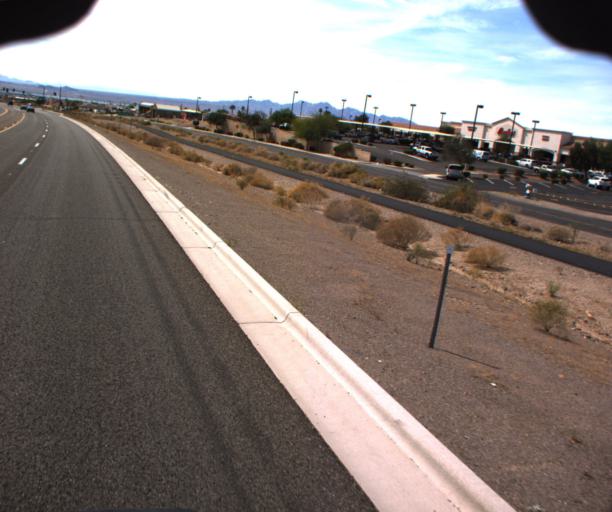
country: US
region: Arizona
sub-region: Mohave County
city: Lake Havasu City
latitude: 34.4577
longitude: -114.2772
